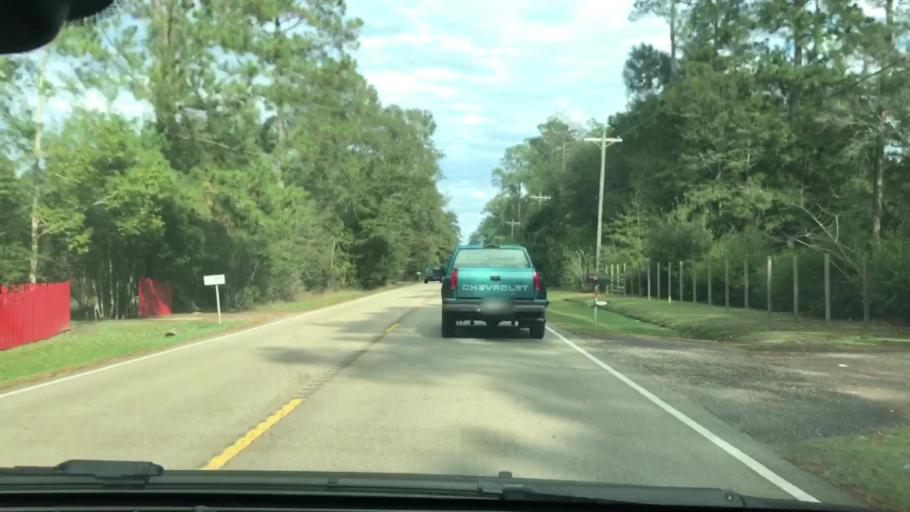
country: US
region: Louisiana
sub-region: Saint Tammany Parish
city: Abita Springs
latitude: 30.4953
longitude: -90.0068
